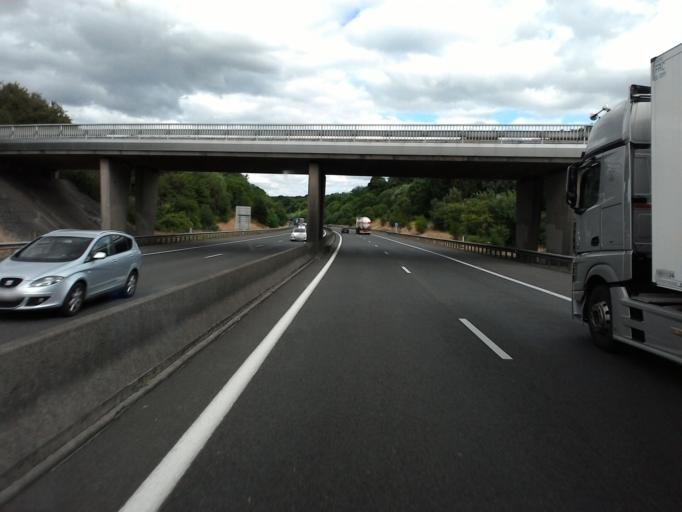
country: LU
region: Luxembourg
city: Capellen
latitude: 49.6347
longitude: 5.9798
